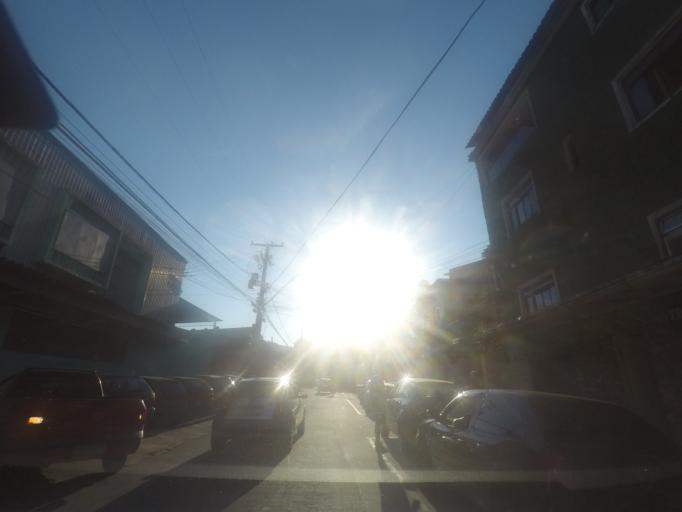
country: BR
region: Rio de Janeiro
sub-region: Petropolis
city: Petropolis
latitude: -22.5261
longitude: -43.1721
